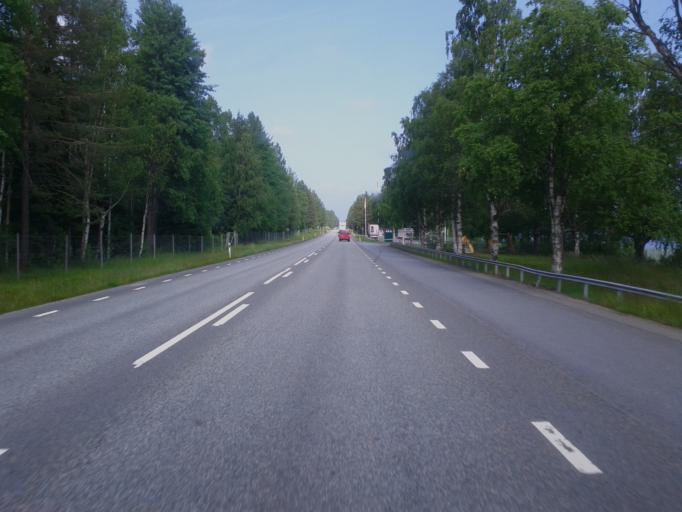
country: SE
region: Vaesterbotten
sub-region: Skelleftea Kommun
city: Burea
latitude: 64.5375
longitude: 21.2575
